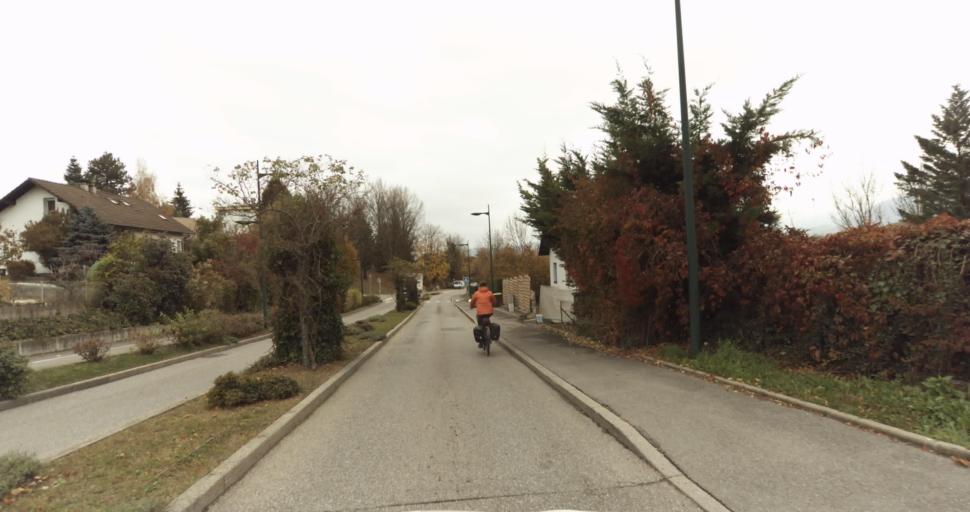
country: FR
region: Rhone-Alpes
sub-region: Departement de la Haute-Savoie
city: Annecy
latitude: 45.8837
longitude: 6.1087
